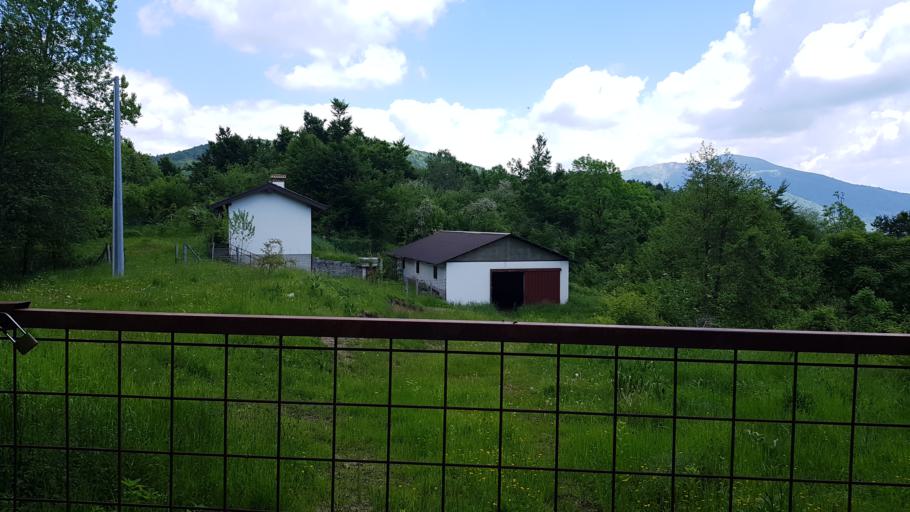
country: IT
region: Friuli Venezia Giulia
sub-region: Provincia di Udine
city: Pulfero
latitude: 46.1933
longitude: 13.4265
